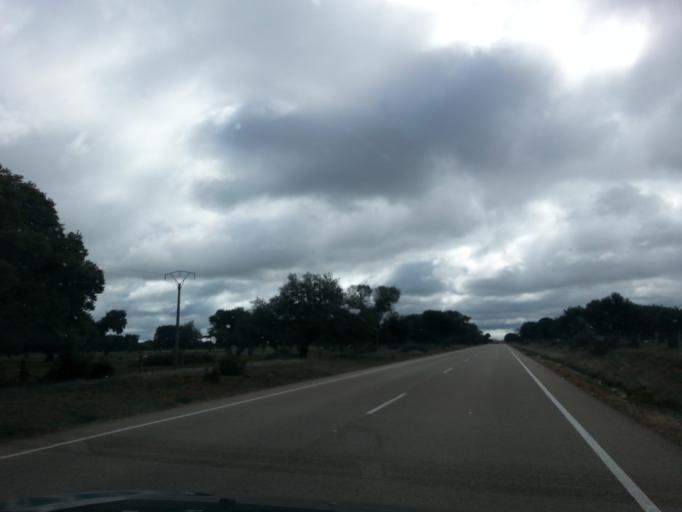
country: ES
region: Castille and Leon
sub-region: Provincia de Salamanca
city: Cabrillas
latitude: 40.7285
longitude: -6.1602
